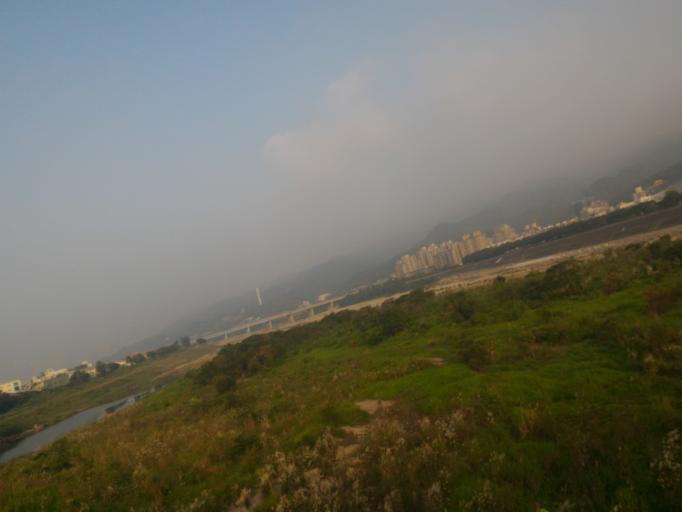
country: TW
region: Taipei
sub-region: Taipei
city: Banqiao
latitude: 24.9660
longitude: 121.4046
